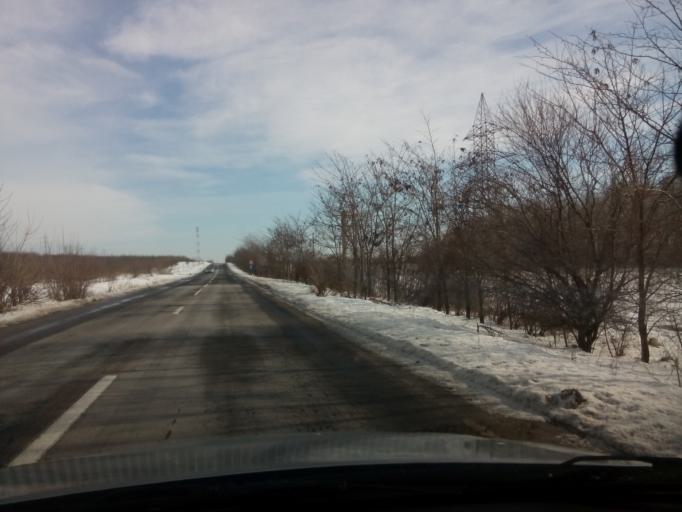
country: RO
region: Calarasi
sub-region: Comuna Budesti
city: Budesti
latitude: 44.2320
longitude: 26.4792
